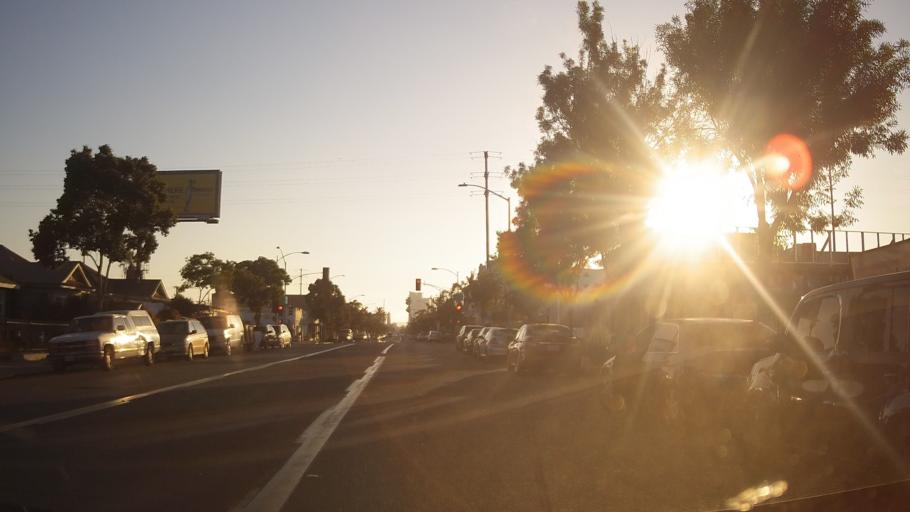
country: US
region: California
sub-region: San Diego County
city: San Diego
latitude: 32.7064
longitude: -117.1330
